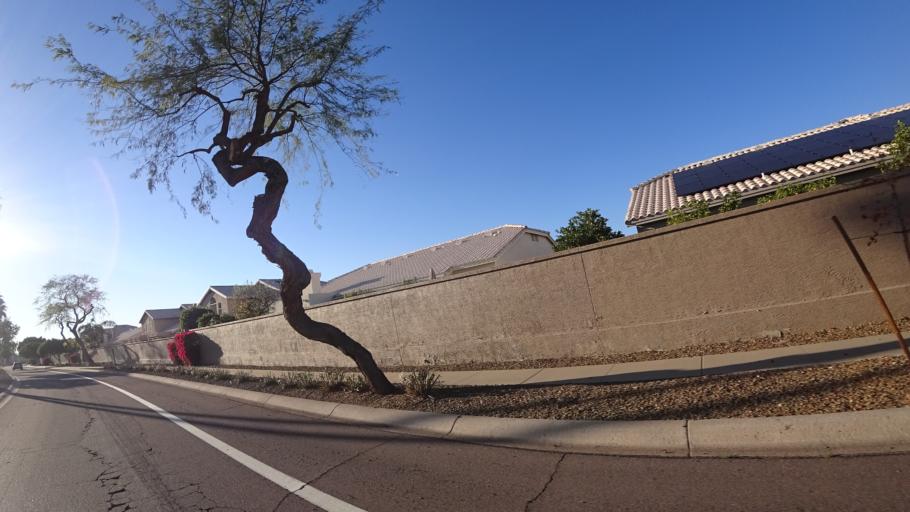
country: US
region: Arizona
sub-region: Maricopa County
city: Peoria
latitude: 33.6827
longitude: -112.1952
